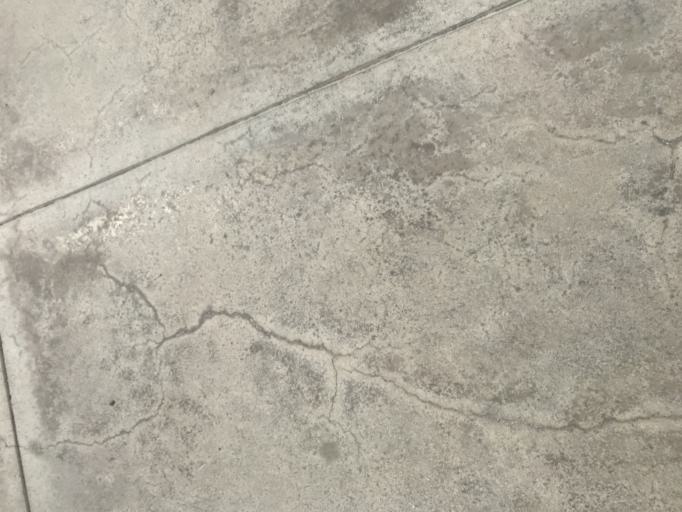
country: TR
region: Istanbul
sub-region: Atasehir
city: Atasehir
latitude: 40.9399
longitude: 29.1081
